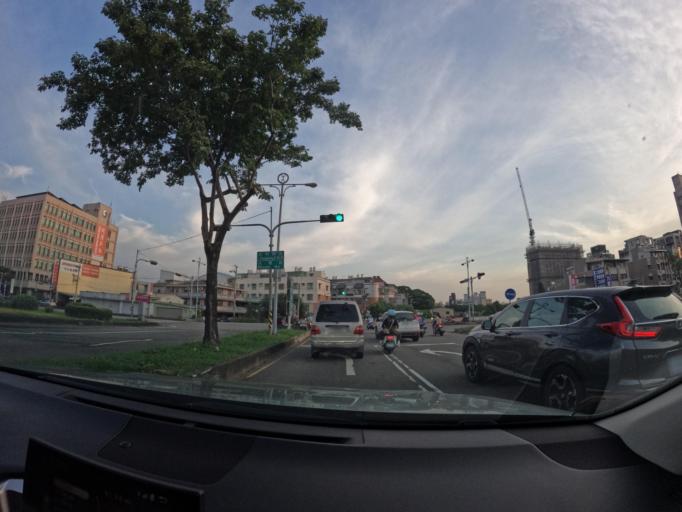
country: TW
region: Taiwan
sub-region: Taichung City
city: Taichung
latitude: 24.1195
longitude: 120.6842
